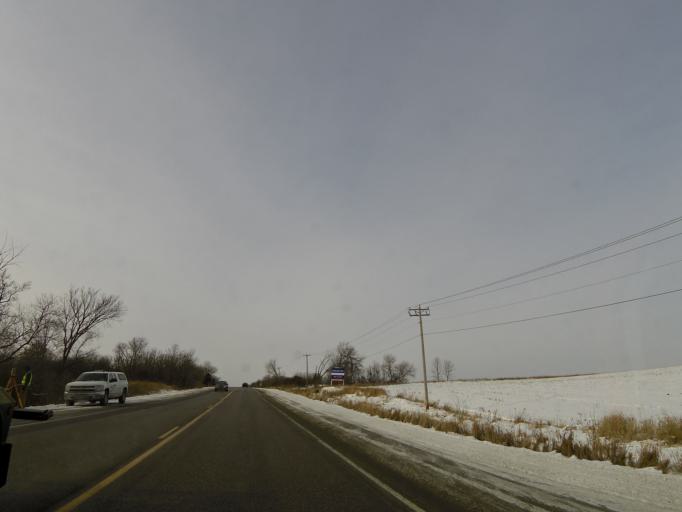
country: US
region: Minnesota
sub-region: Carver County
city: Victoria
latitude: 44.8913
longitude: -93.6925
